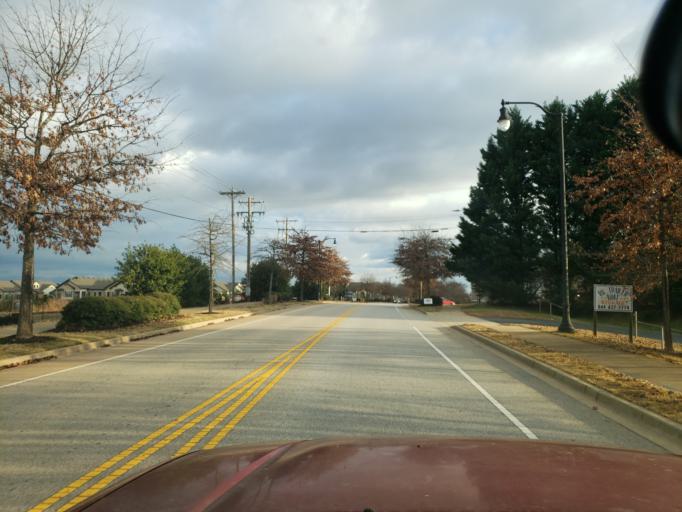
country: US
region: South Carolina
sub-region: Greenville County
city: Mauldin
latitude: 34.8352
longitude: -82.3341
